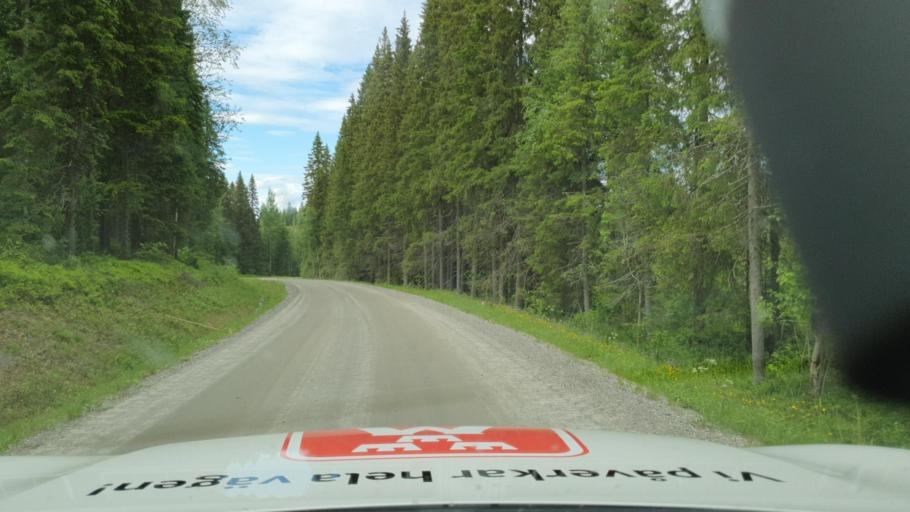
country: SE
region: Vaesterbotten
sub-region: Norsjo Kommun
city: Norsjoe
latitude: 64.8039
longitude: 19.6645
